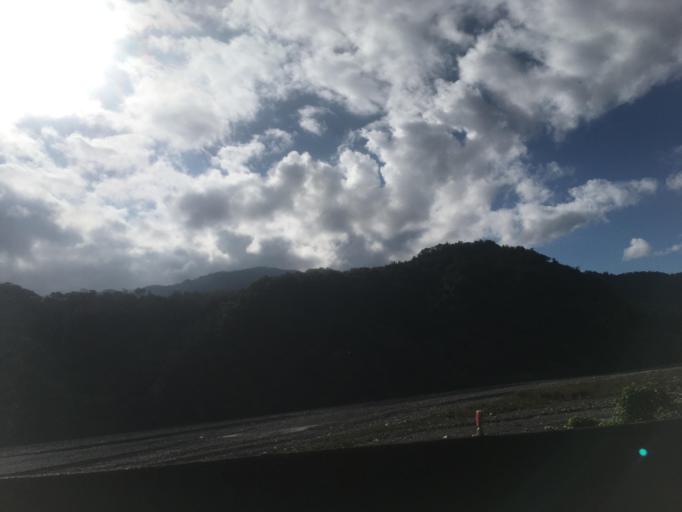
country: TW
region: Taiwan
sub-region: Yilan
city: Yilan
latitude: 24.6415
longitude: 121.5602
